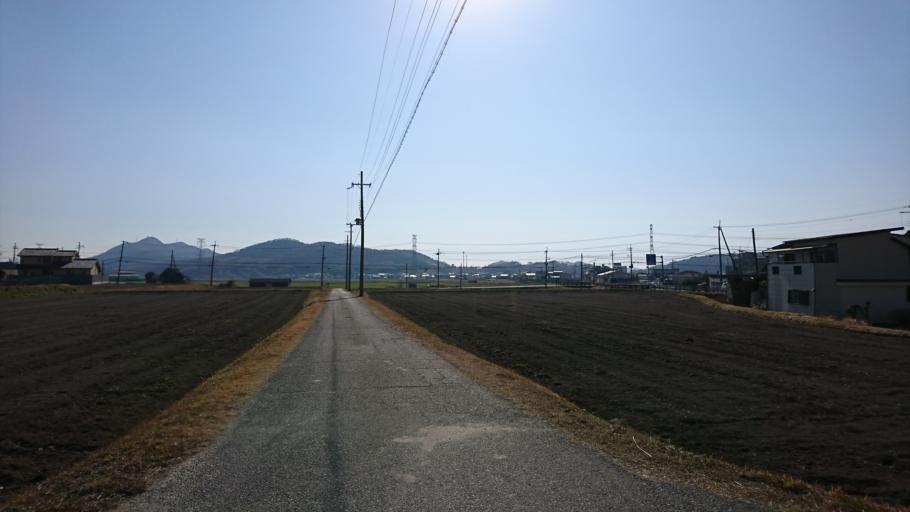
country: JP
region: Hyogo
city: Kakogawacho-honmachi
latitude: 34.8343
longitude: 134.8407
